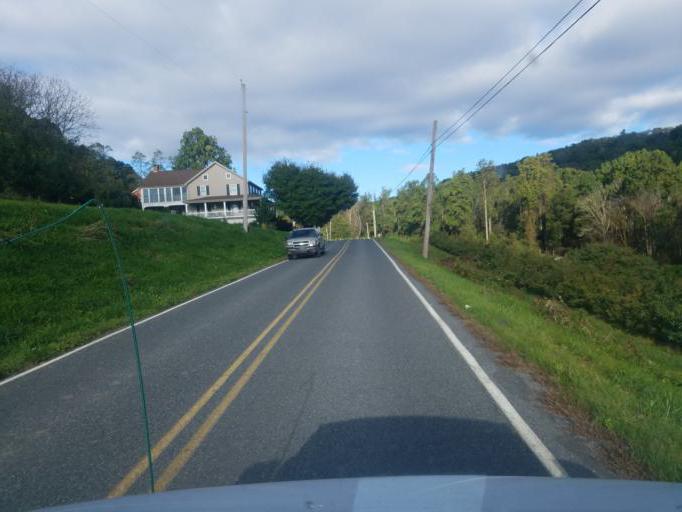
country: US
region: Pennsylvania
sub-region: Adams County
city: Carroll Valley
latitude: 39.8919
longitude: -77.3902
